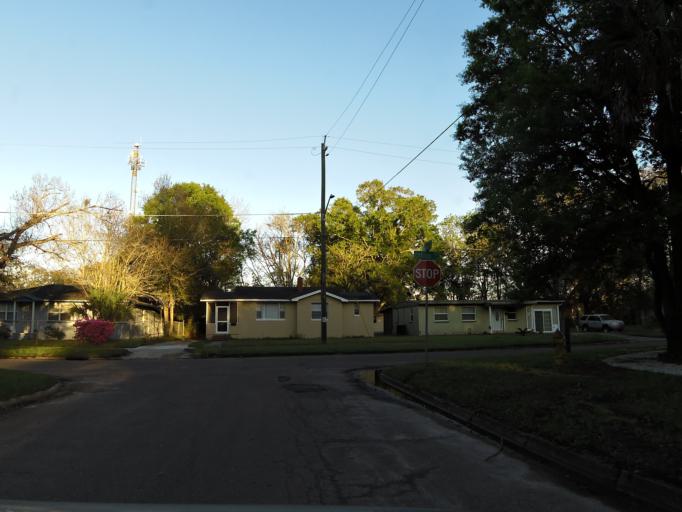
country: US
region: Florida
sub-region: Duval County
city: Jacksonville
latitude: 30.3394
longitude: -81.7124
